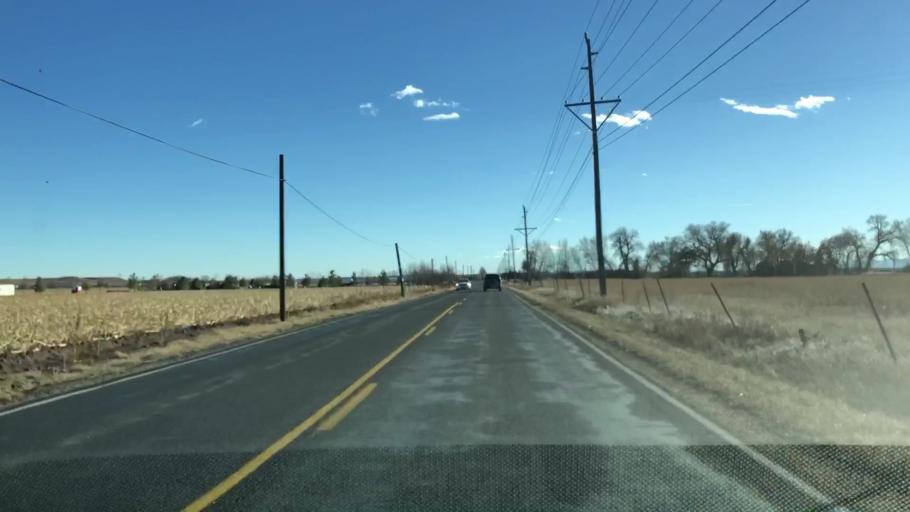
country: US
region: Colorado
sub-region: Larimer County
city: Fort Collins
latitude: 40.5586
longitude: -104.9822
